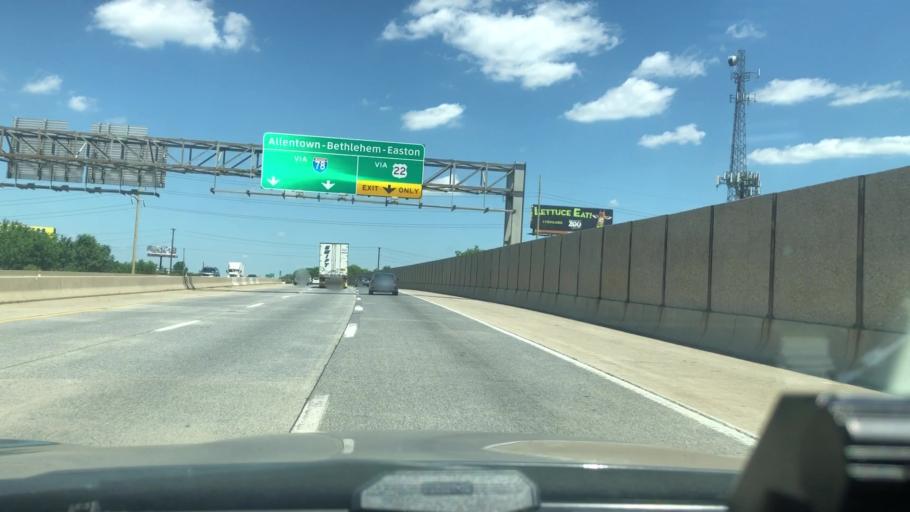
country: US
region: Pennsylvania
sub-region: Lehigh County
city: Trexlertown
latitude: 40.5835
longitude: -75.6047
